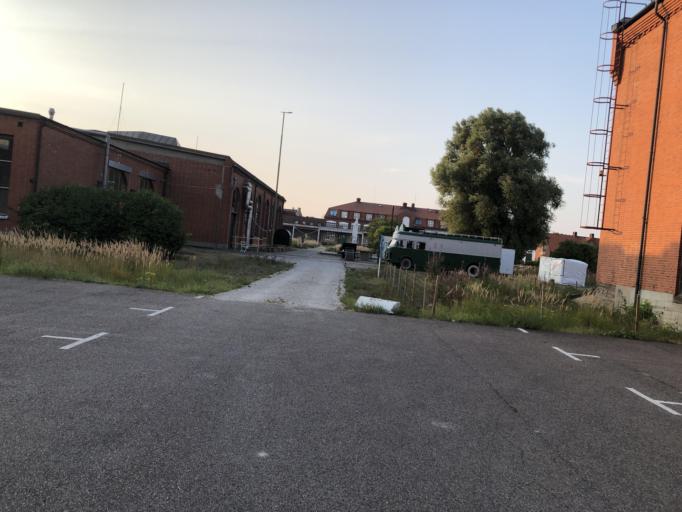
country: SE
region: Skane
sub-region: Burlovs Kommun
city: Arloev
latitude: 55.6048
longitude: 13.0430
